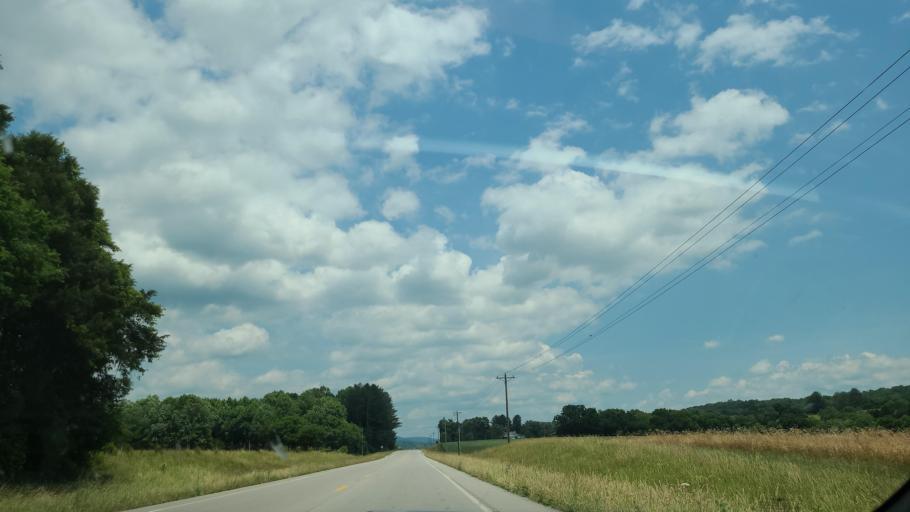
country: US
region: Tennessee
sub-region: Bledsoe County
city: Pikeville
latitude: 35.6267
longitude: -85.1793
